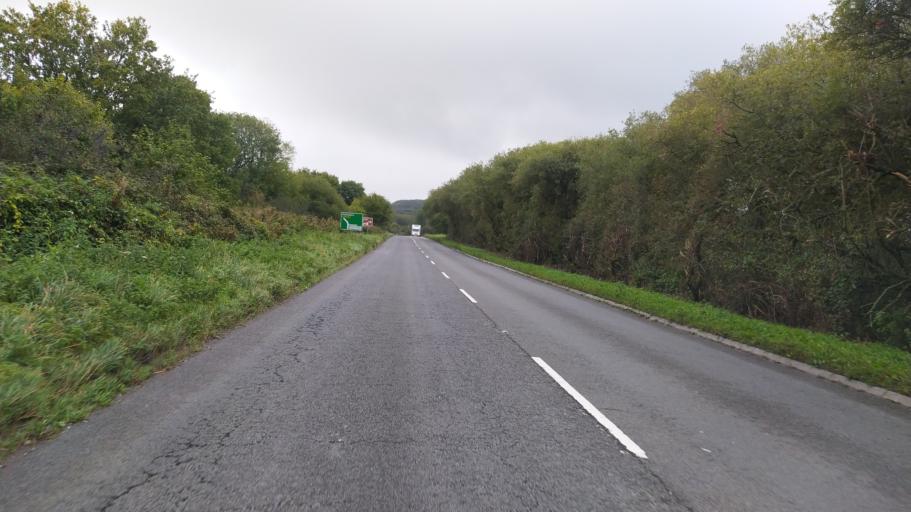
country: GB
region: England
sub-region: Dorset
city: Shaftesbury
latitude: 51.0431
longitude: -2.1849
